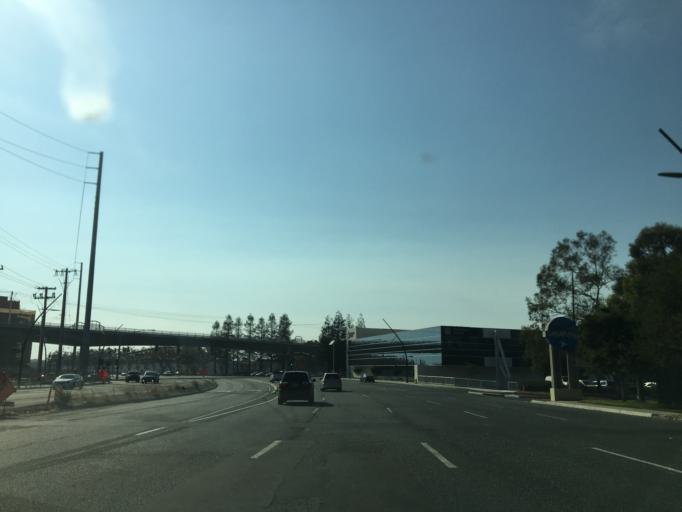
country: US
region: California
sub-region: Santa Clara County
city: Milpitas
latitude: 37.4110
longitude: -121.8923
